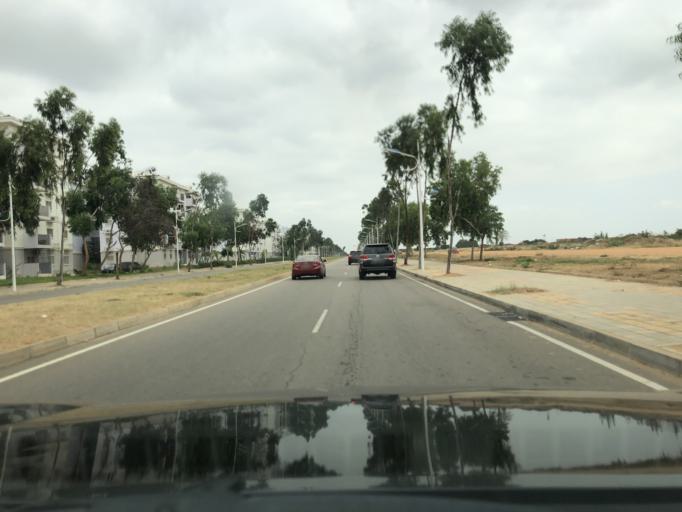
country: AO
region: Luanda
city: Luanda
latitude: -8.9911
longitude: 13.2802
